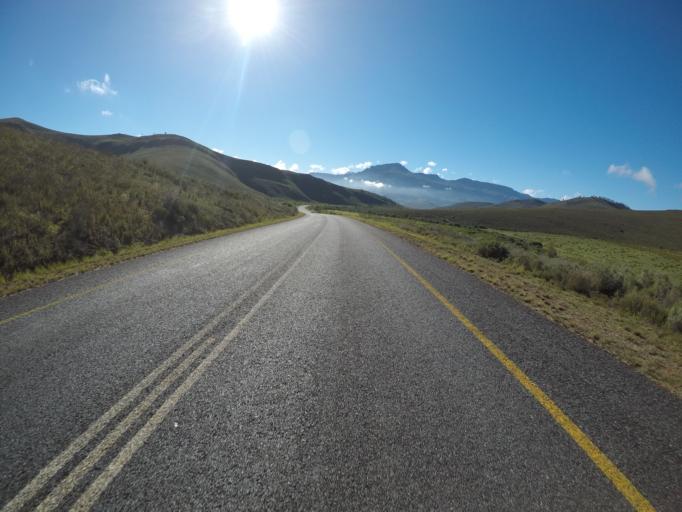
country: ZA
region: Western Cape
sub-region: Overberg District Municipality
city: Caledon
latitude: -34.0875
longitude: 19.5519
